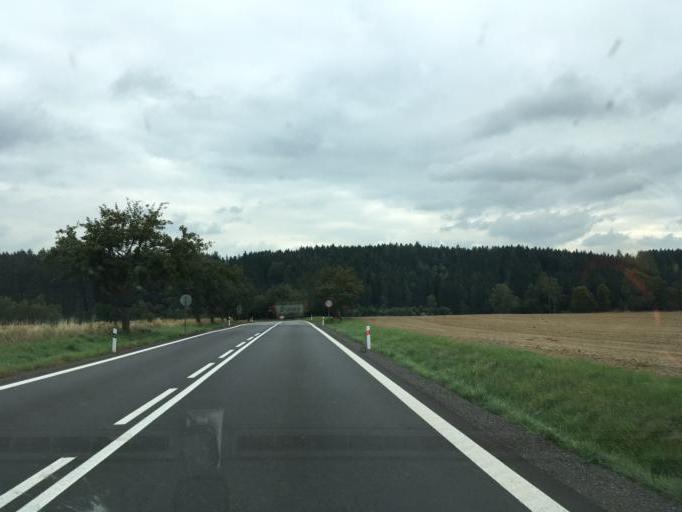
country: CZ
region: Central Bohemia
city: Cechtice
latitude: 49.5775
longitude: 15.0928
